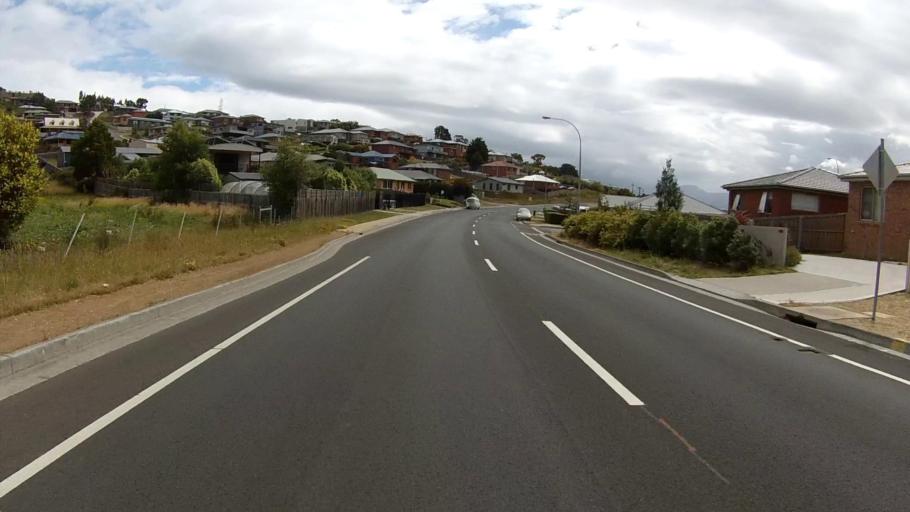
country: AU
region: Tasmania
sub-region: Clarence
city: Warrane
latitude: -42.8572
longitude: 147.4123
